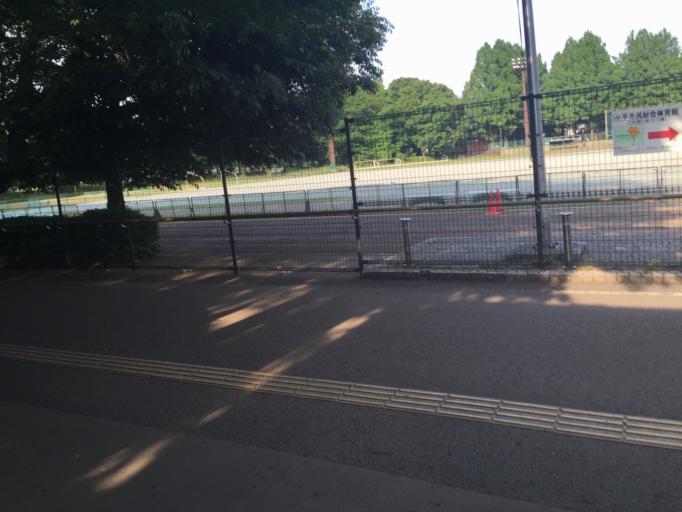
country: JP
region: Tokyo
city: Kokubunji
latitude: 35.7234
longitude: 139.4614
